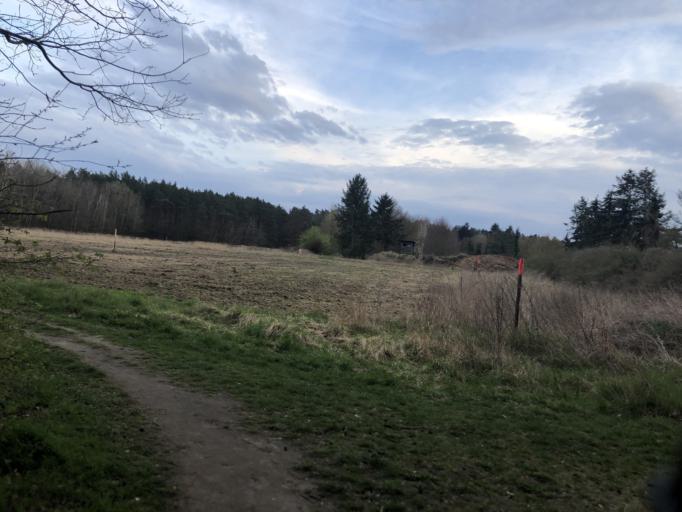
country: DE
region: Berlin
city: Frohnau
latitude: 52.6519
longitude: 13.2887
